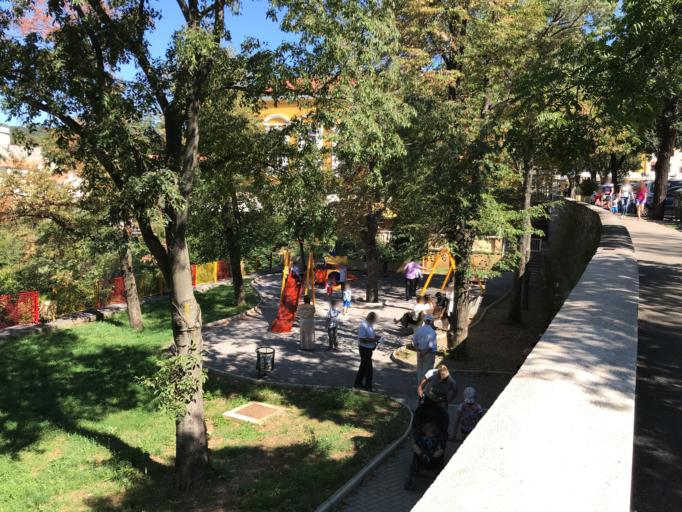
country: HR
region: Primorsko-Goranska
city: Drenova
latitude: 45.3307
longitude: 14.4559
